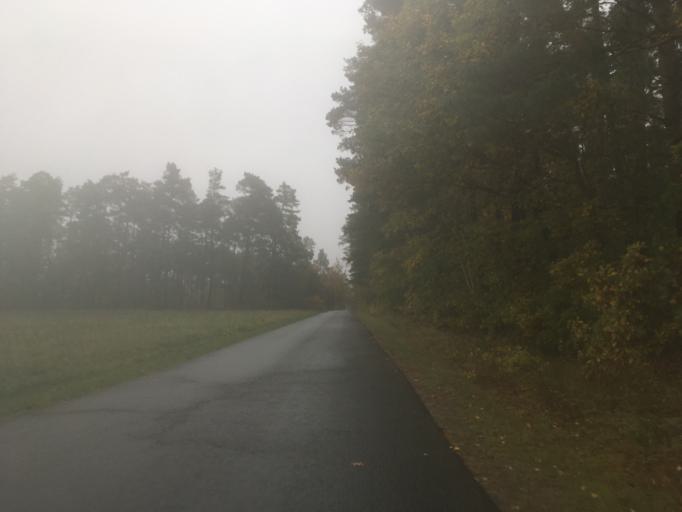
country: DE
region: Brandenburg
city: Neu Zauche
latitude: 52.0308
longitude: 14.0332
